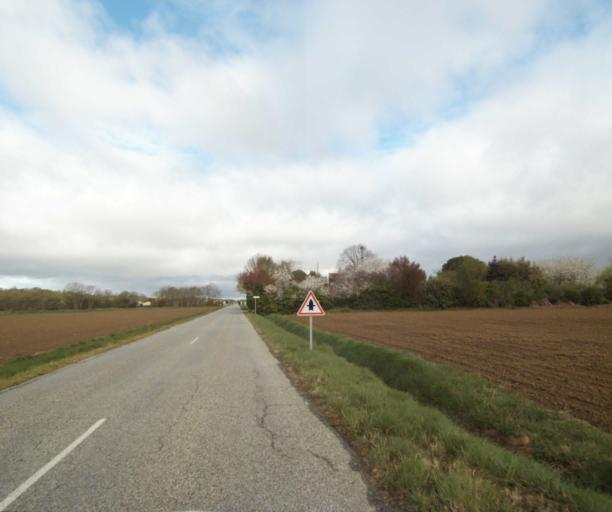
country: FR
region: Midi-Pyrenees
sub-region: Departement de l'Ariege
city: Saverdun
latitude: 43.2549
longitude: 1.5420
